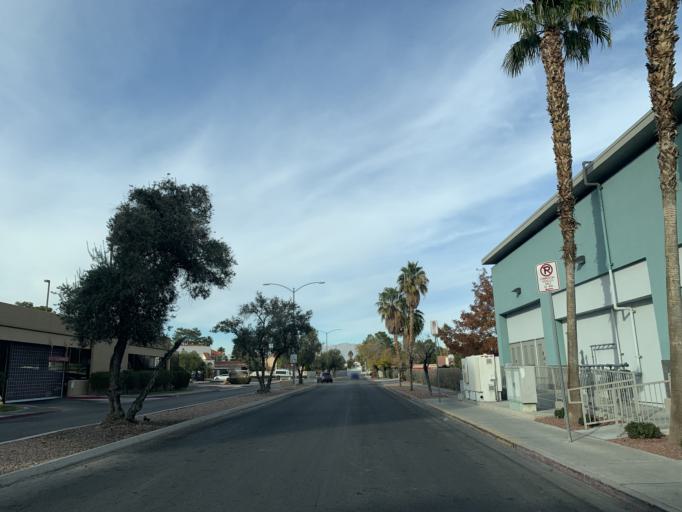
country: US
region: Nevada
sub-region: Clark County
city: Las Vegas
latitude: 36.1451
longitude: -115.1775
